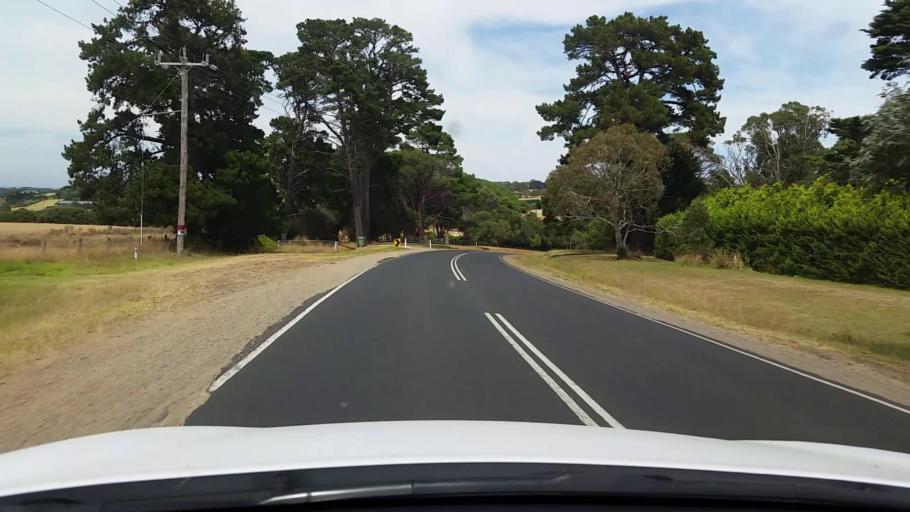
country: AU
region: Victoria
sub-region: Mornington Peninsula
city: Merricks
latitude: -38.4474
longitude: 145.0321
